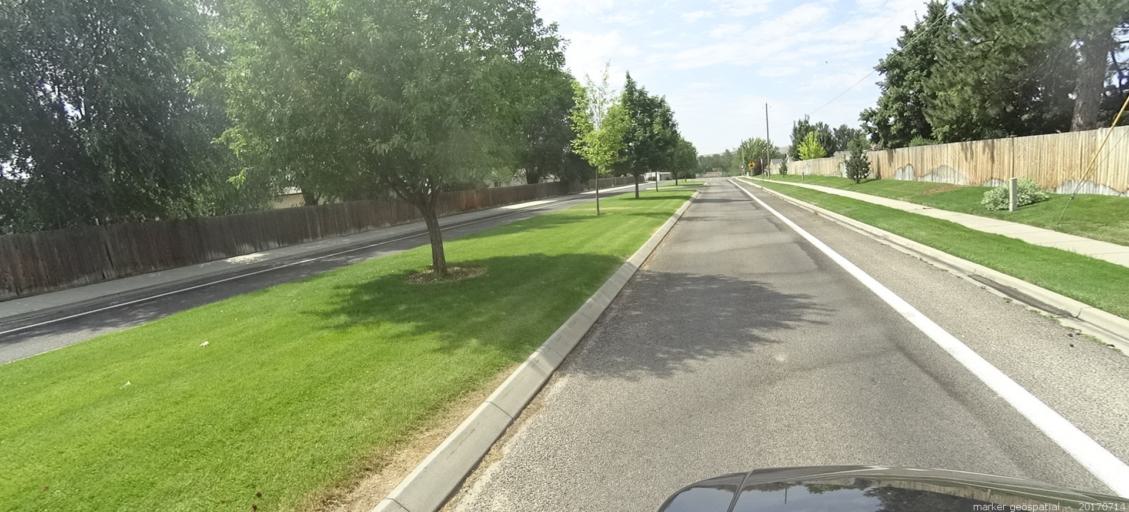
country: US
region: Idaho
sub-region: Ada County
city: Kuna
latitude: 43.4936
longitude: -116.4337
